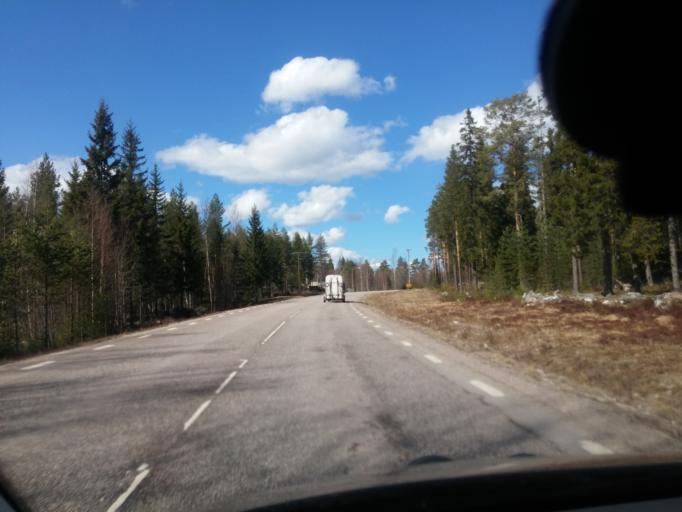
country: SE
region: Gaevleborg
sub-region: Ovanakers Kommun
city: Edsbyn
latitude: 61.2548
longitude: 15.8857
